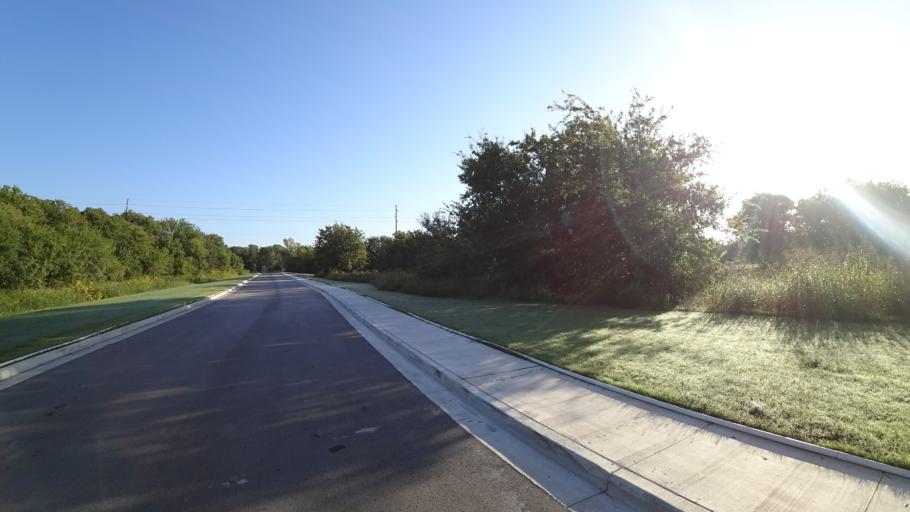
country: US
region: Texas
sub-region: Travis County
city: Wells Branch
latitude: 30.3633
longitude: -97.6879
